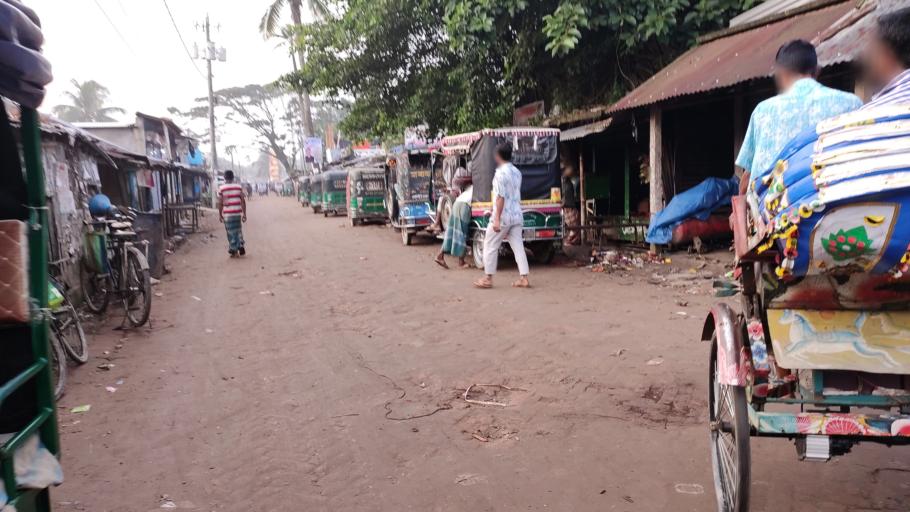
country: BD
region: Dhaka
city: Netrakona
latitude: 24.7166
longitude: 90.9469
